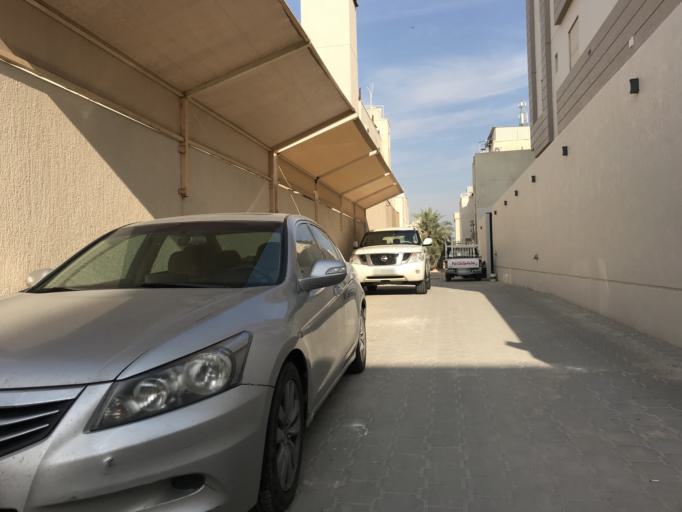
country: KW
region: Muhafazat Hawalli
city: Ar Rumaythiyah
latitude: 29.3036
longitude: 48.0745
